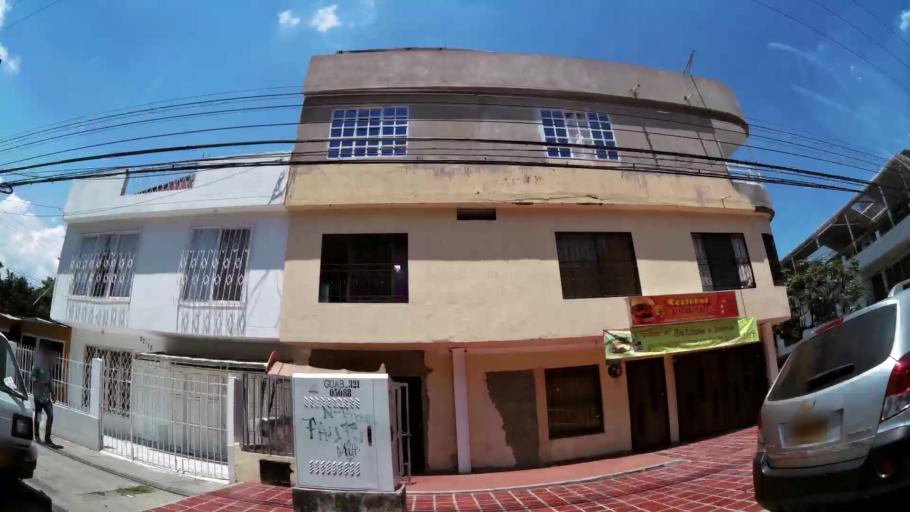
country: CO
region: Valle del Cauca
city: Cali
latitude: 3.4484
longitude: -76.4914
